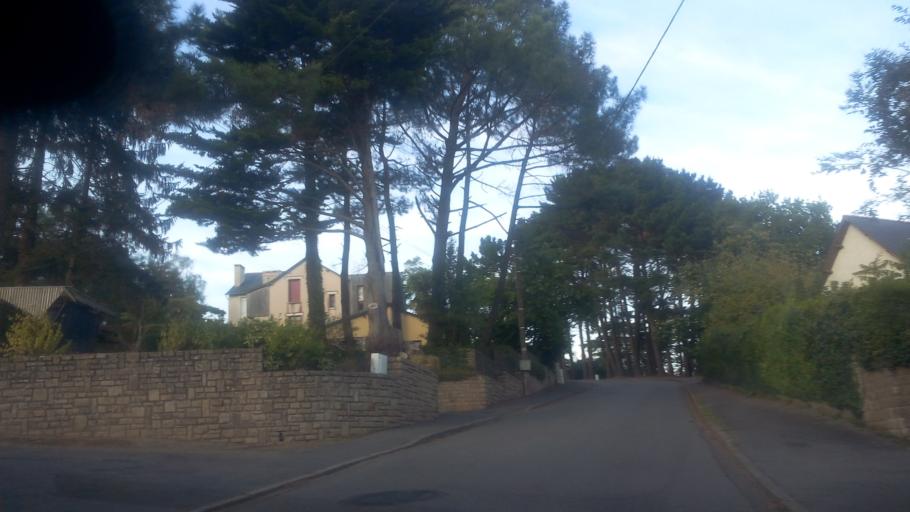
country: FR
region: Brittany
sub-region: Departement d'Ille-et-Vilaine
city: Redon
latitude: 47.6561
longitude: -2.0901
